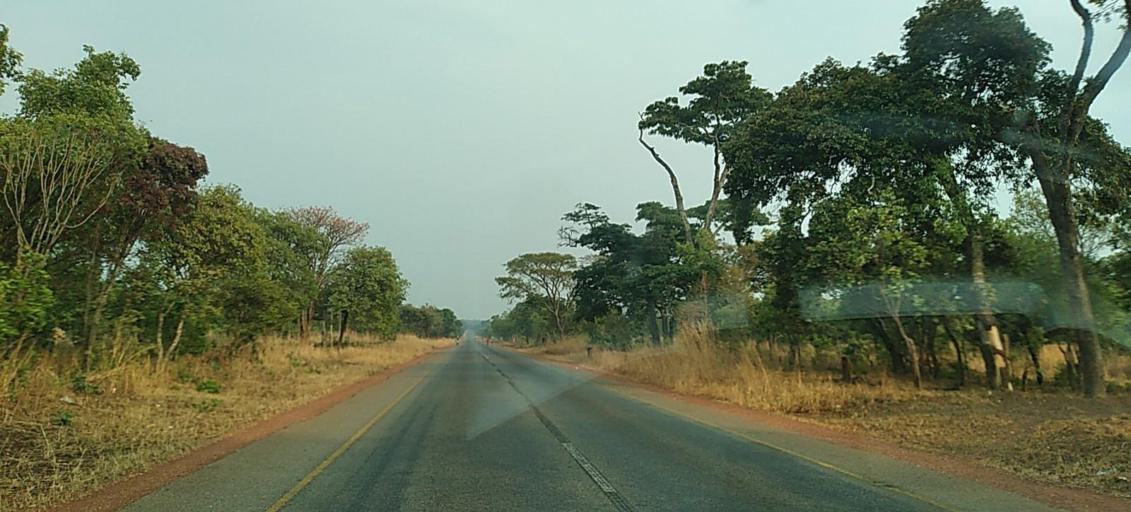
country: ZM
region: North-Western
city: Solwezi
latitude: -12.3895
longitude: 26.0351
